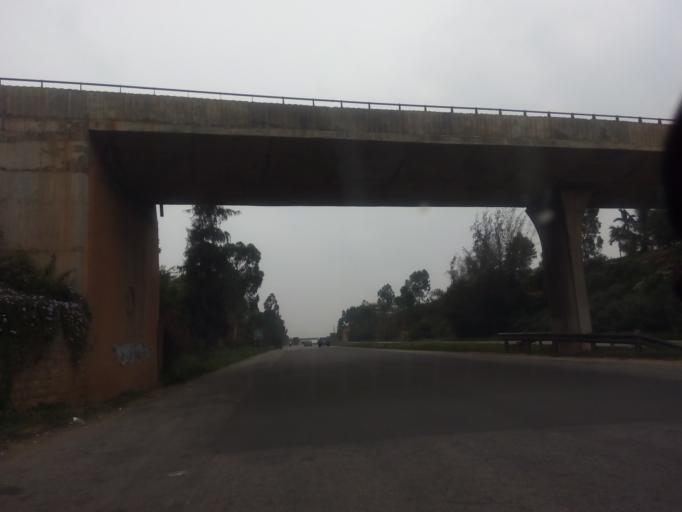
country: IN
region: Karnataka
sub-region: Bangalore Urban
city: Bangalore
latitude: 12.8595
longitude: 77.6543
